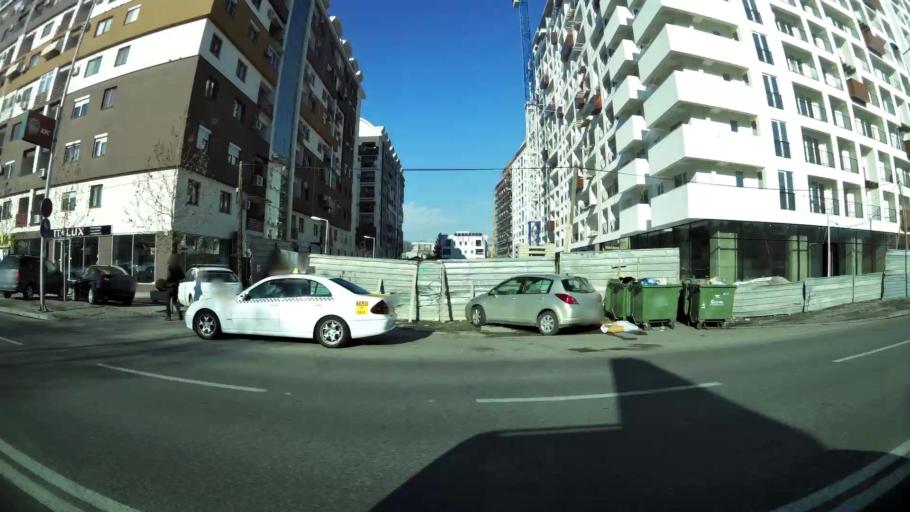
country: MK
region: Karpos
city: Skopje
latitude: 41.9973
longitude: 21.3978
